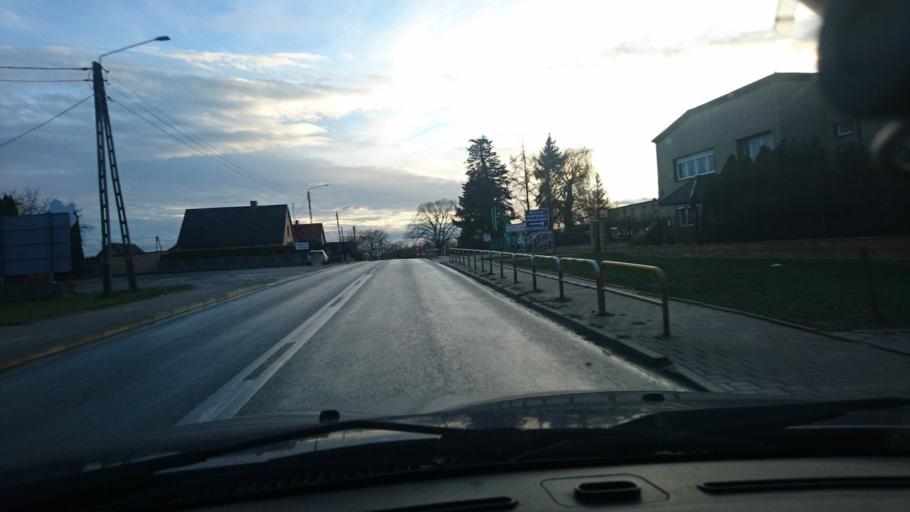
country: PL
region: Opole Voivodeship
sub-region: Powiat kluczborski
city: Byczyna
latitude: 51.1111
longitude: 18.2078
